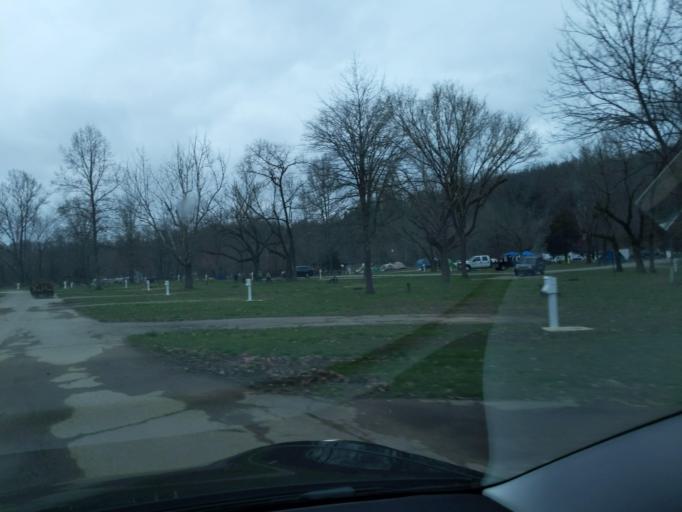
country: US
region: Kentucky
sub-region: Clark County
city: Winchester
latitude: 37.9022
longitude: -84.2679
